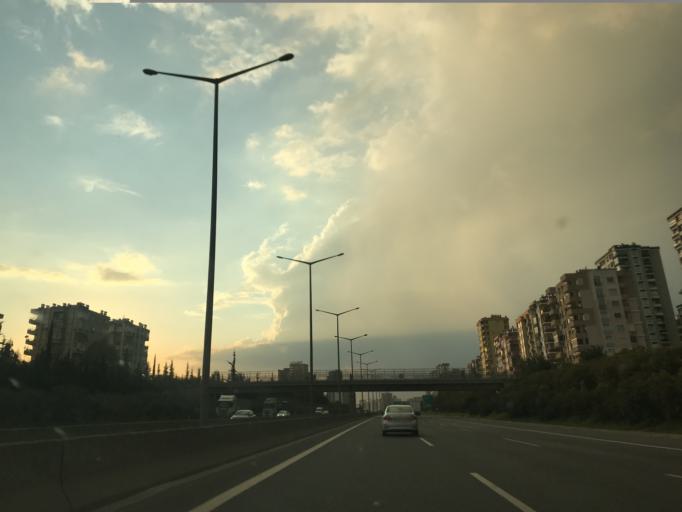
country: TR
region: Adana
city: Seyhan
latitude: 37.0307
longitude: 35.2675
